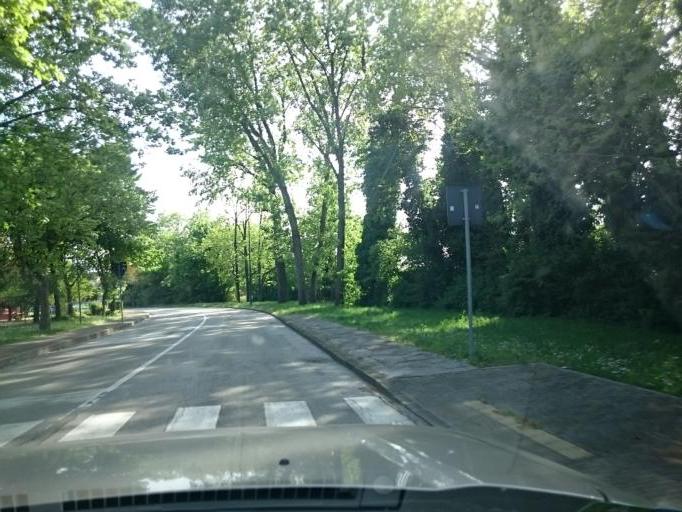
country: IT
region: Veneto
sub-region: Provincia di Venezia
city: Campalto
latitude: 45.4817
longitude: 12.2854
